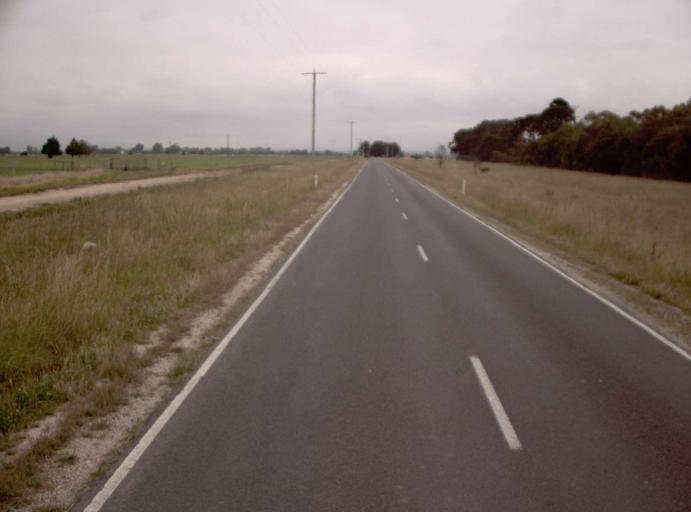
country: AU
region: Victoria
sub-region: Wellington
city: Heyfield
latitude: -38.0273
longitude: 146.7656
